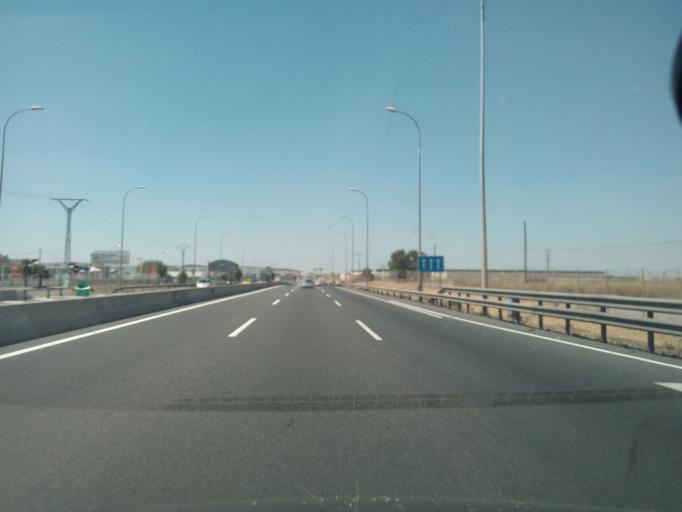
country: ES
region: Castille-La Mancha
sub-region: Province of Toledo
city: Sesena
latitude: 40.1102
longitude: -3.6488
